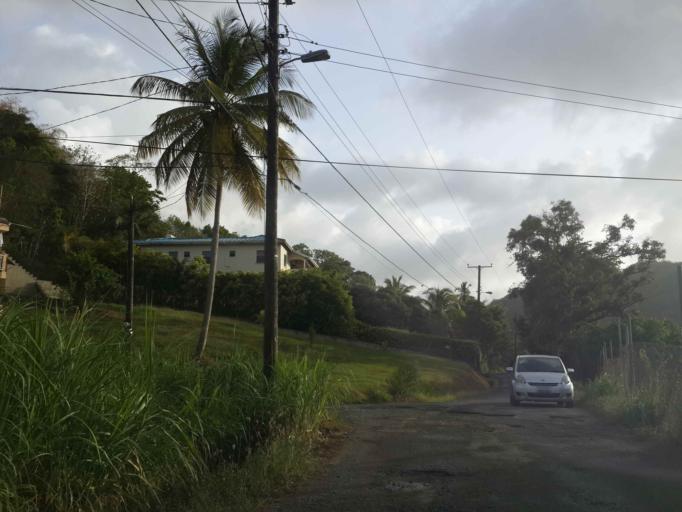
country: LC
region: Castries Quarter
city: Bisee
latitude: 14.0229
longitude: -60.9583
